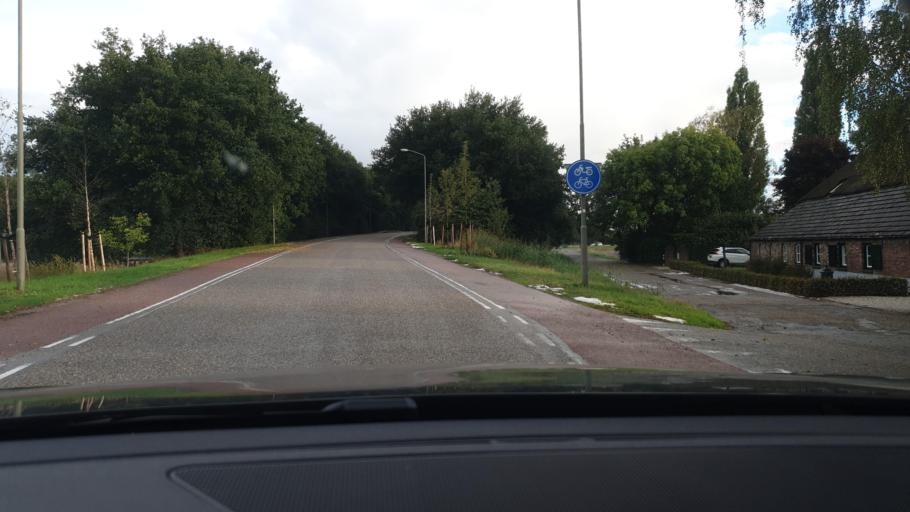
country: NL
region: North Brabant
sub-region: Gemeente Landerd
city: Schaijk
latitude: 51.7859
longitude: 5.6421
